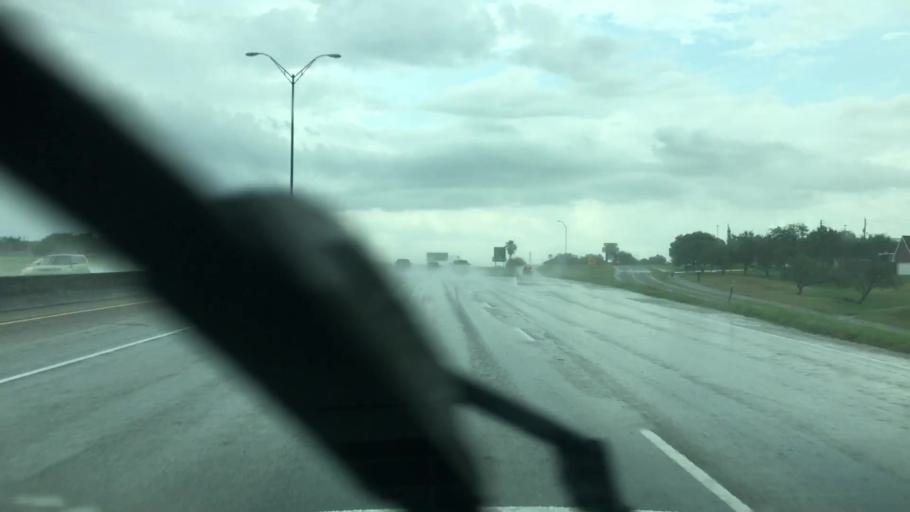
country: US
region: Texas
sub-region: San Patricio County
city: Odem
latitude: 27.8558
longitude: -97.5983
